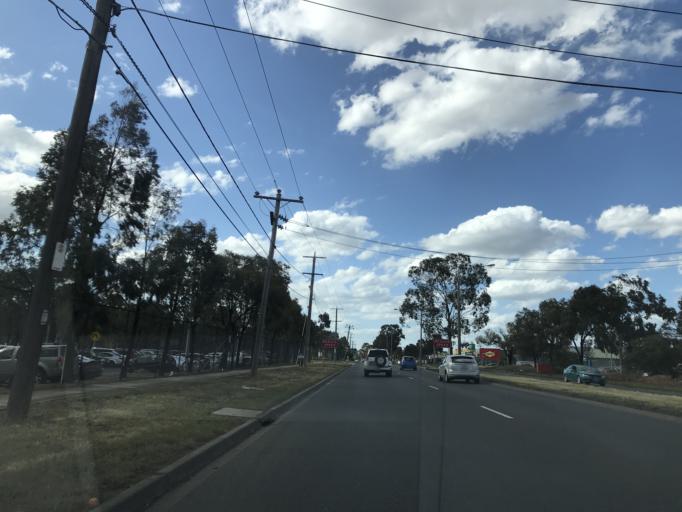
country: AU
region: Victoria
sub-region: Brimbank
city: Sunshine West
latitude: -37.8089
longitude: 144.8181
